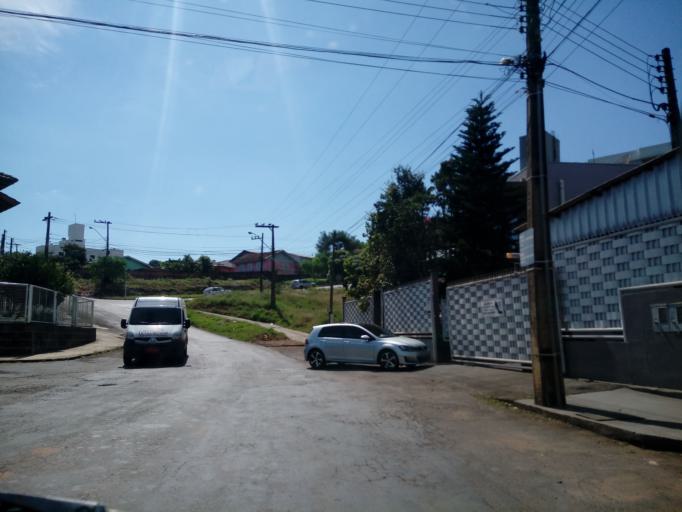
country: BR
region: Santa Catarina
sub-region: Chapeco
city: Chapeco
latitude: -27.1134
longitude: -52.6238
